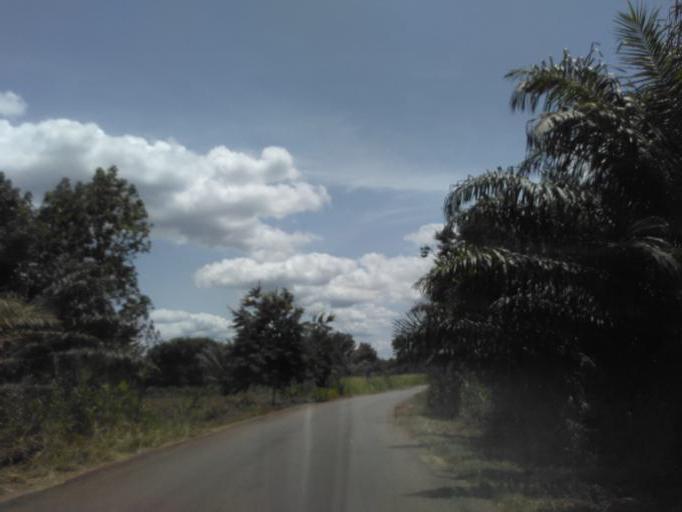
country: GH
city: Akropong
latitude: 6.0994
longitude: -0.1031
